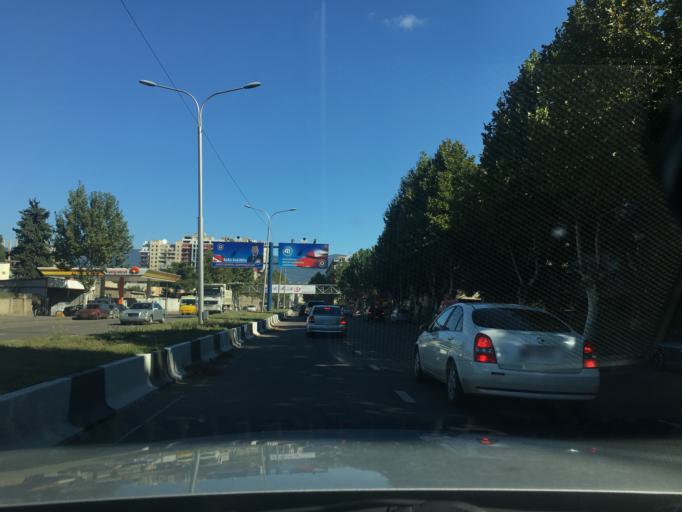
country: GE
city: Zahesi
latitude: 41.7684
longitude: 44.7919
